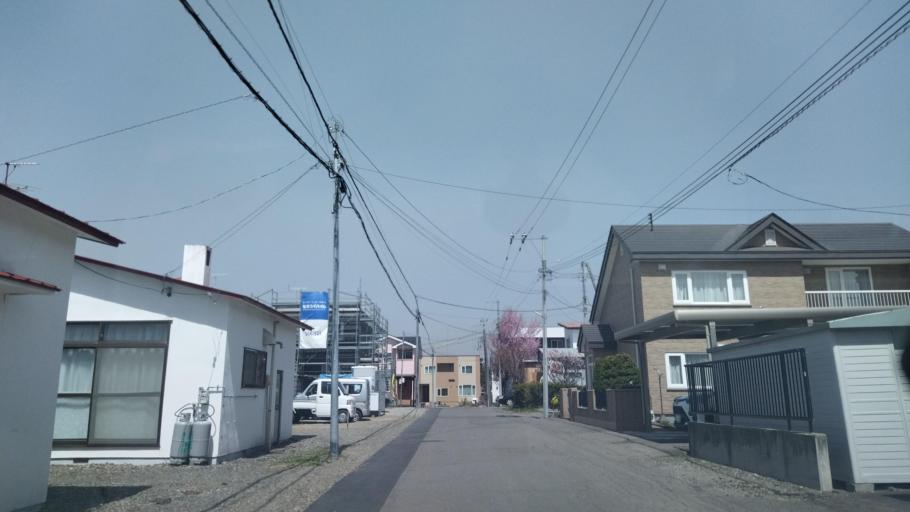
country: JP
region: Hokkaido
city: Obihiro
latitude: 42.9365
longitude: 143.1870
